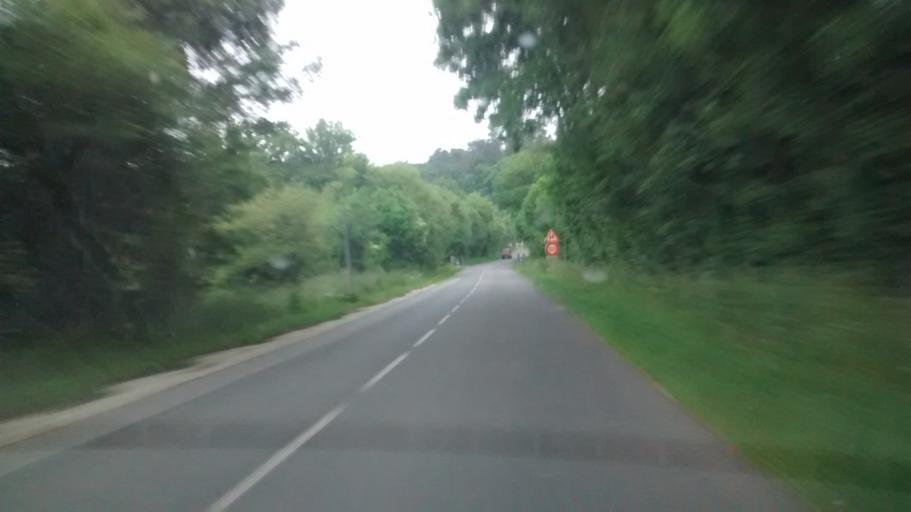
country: FR
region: Brittany
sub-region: Departement du Morbihan
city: Saint-Martin-sur-Oust
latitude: 47.7424
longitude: -2.2675
